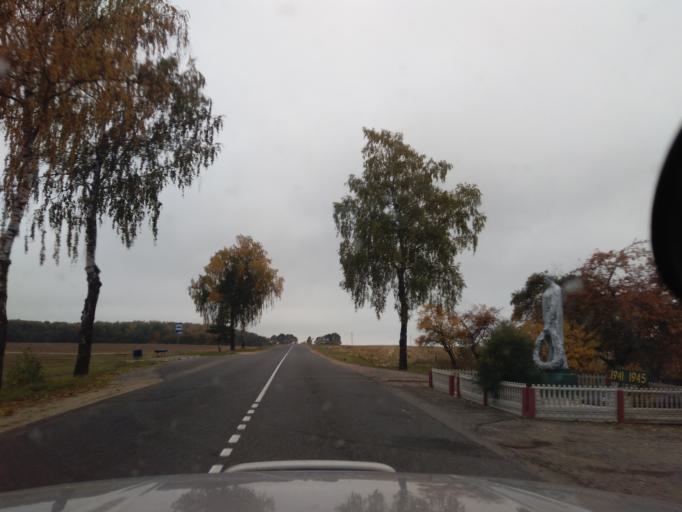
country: BY
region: Minsk
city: Kapyl'
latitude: 53.1498
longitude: 27.1993
